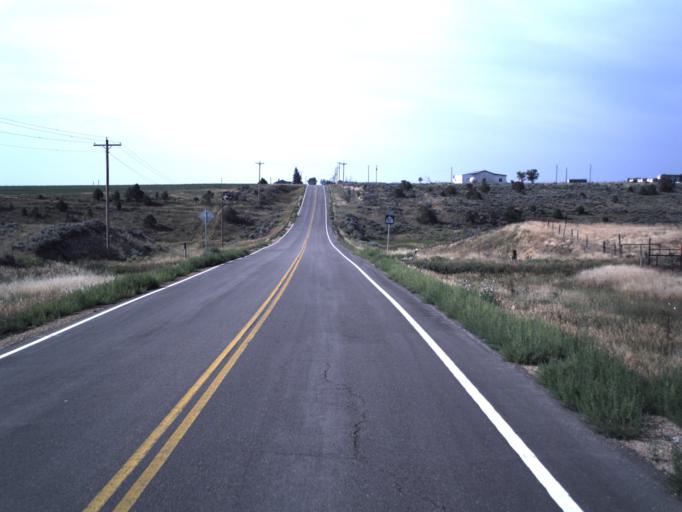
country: US
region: Utah
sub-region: Duchesne County
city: Duchesne
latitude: 40.3454
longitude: -110.4079
